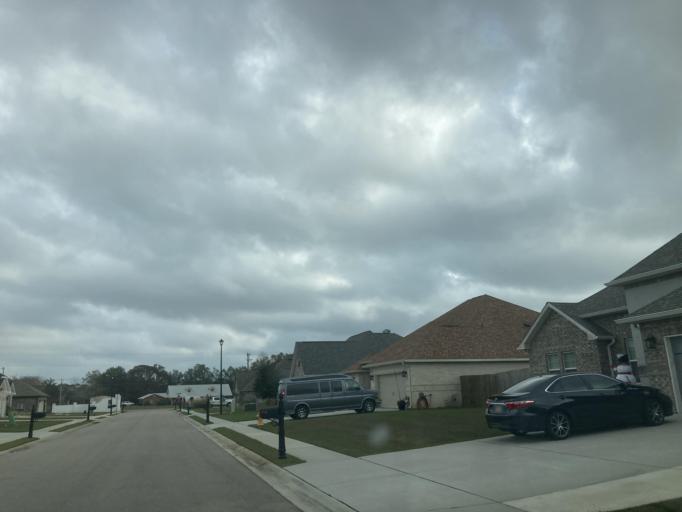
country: US
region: Mississippi
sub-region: Jackson County
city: Latimer
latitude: 30.5050
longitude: -88.9669
